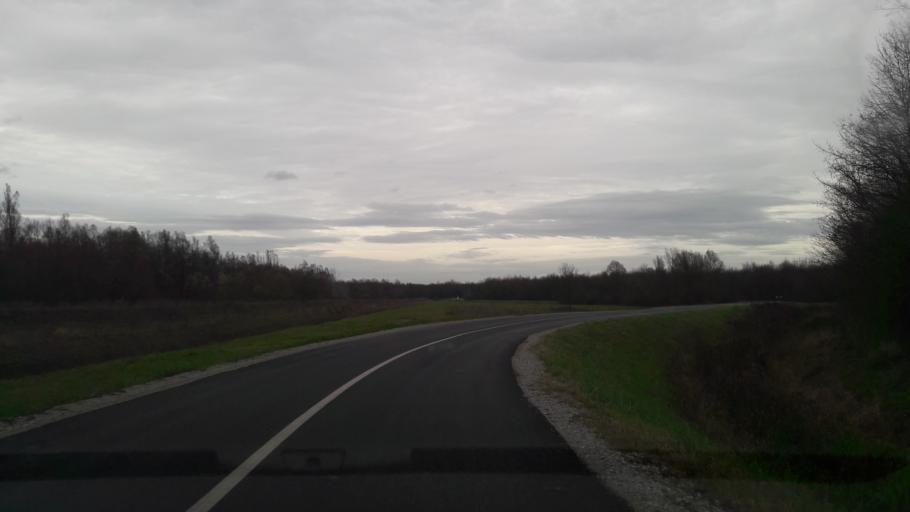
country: HR
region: Osjecko-Baranjska
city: Velimirovac
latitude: 45.6225
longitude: 18.0817
